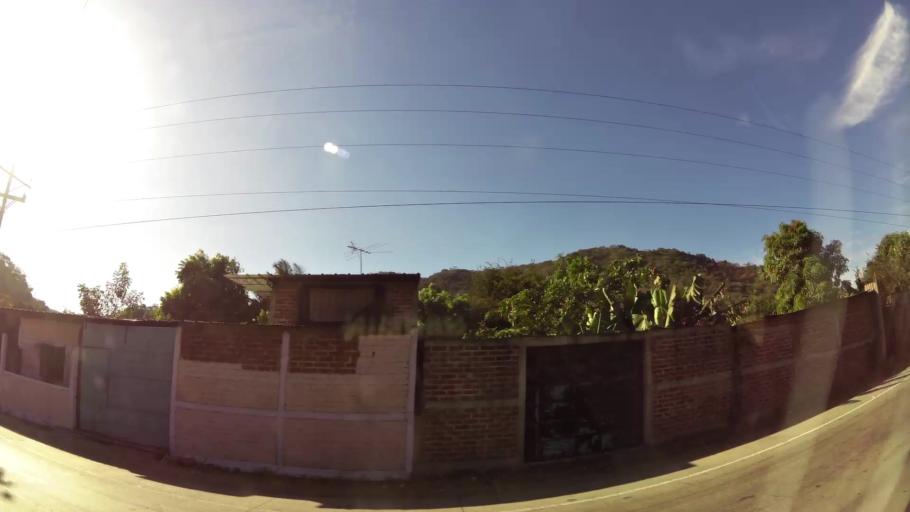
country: SV
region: Santa Ana
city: Santa Ana
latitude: 14.0486
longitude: -89.5172
